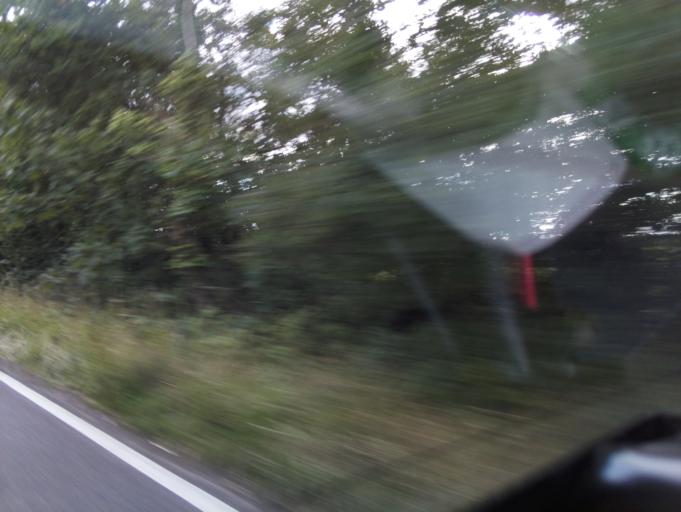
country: GB
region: England
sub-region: Devon
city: Honiton
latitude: 50.7700
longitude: -3.2115
